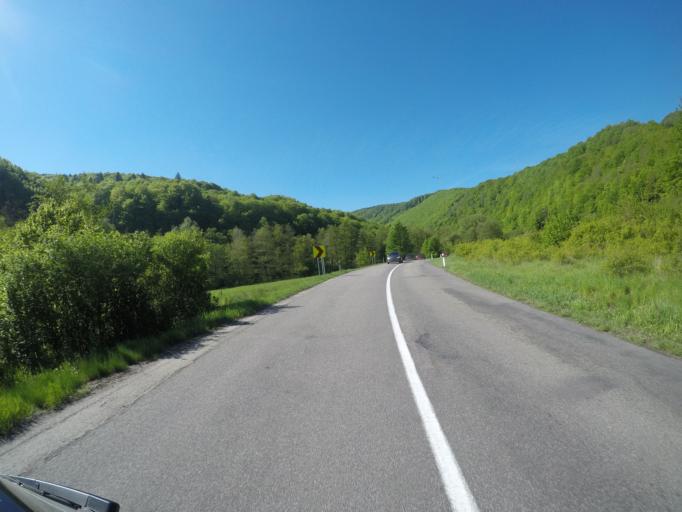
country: SK
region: Banskobystricky
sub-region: Okres Banska Bystrica
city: Banska Stiavnica
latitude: 48.5512
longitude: 19.0059
